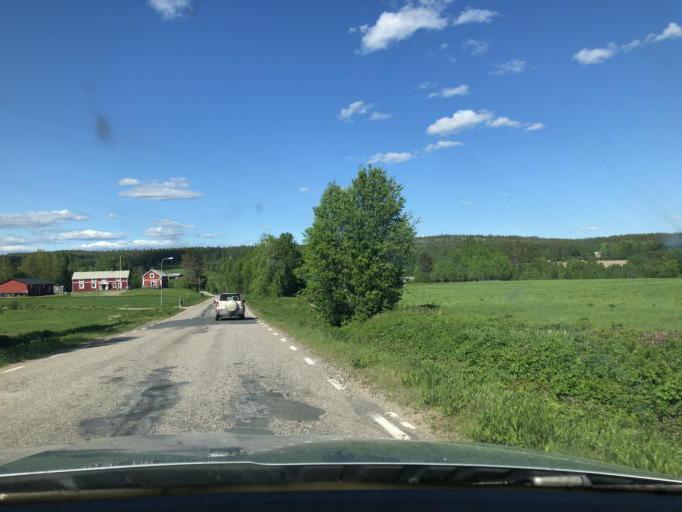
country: SE
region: Norrbotten
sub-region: Kalix Kommun
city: Kalix
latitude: 65.9882
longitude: 23.1464
